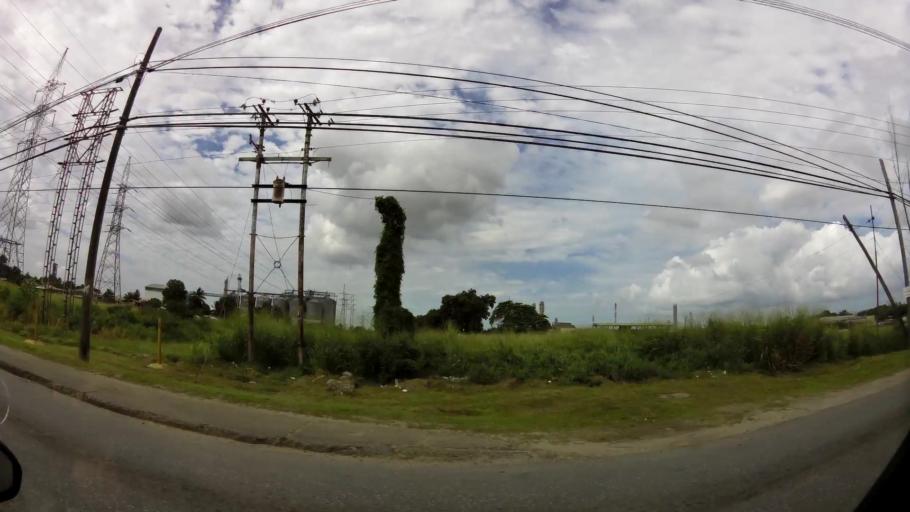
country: TT
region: Couva-Tabaquite-Talparo
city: Couva
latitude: 10.4127
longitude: -61.4711
